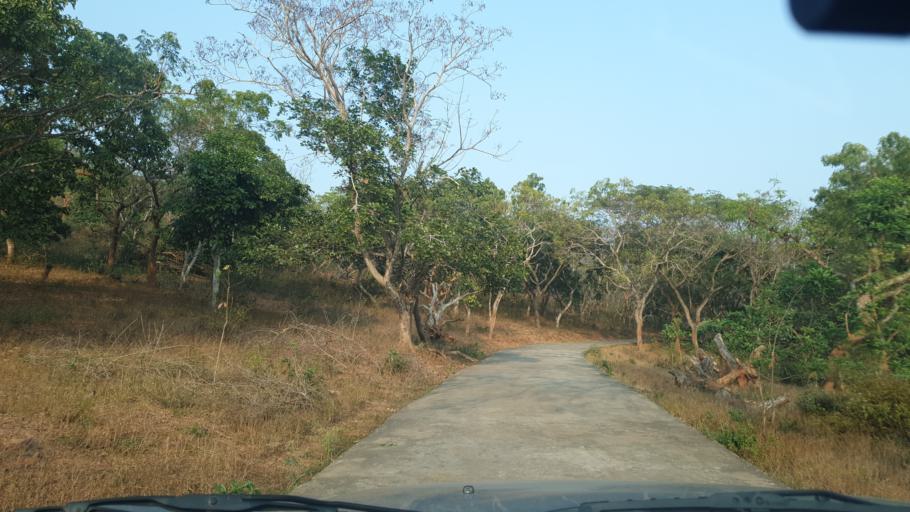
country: IN
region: Andhra Pradesh
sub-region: Srikakulam
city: Narasannapeta
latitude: 18.3319
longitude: 84.0425
